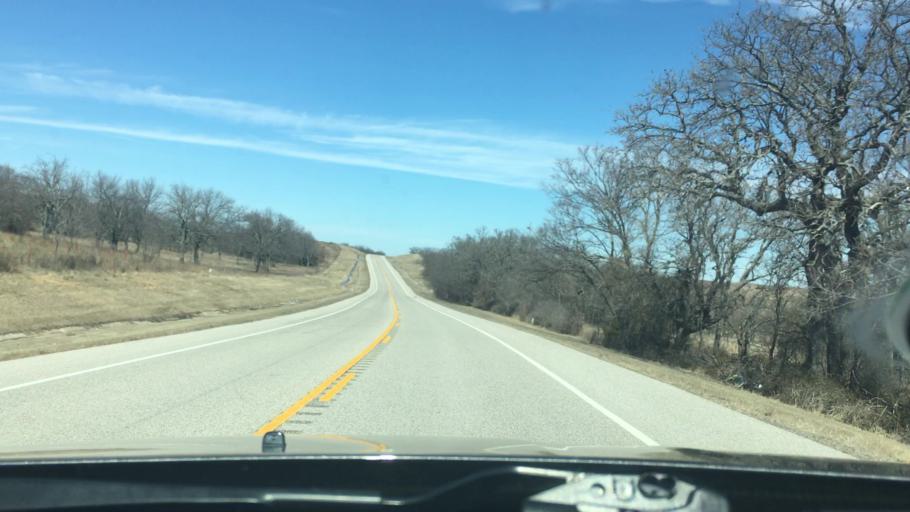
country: US
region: Oklahoma
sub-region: Carter County
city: Dickson
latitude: 34.3358
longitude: -96.9509
